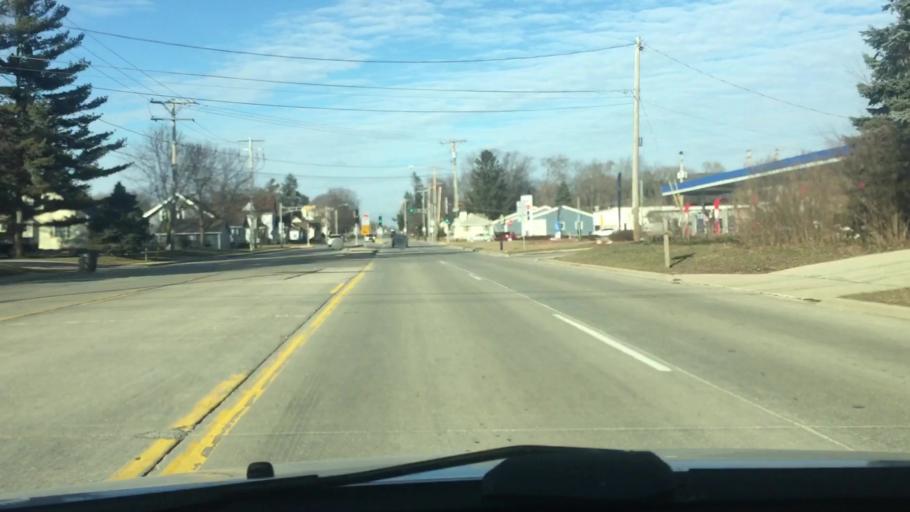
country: US
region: Wisconsin
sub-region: Waukesha County
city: Sussex
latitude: 43.1278
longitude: -88.2096
